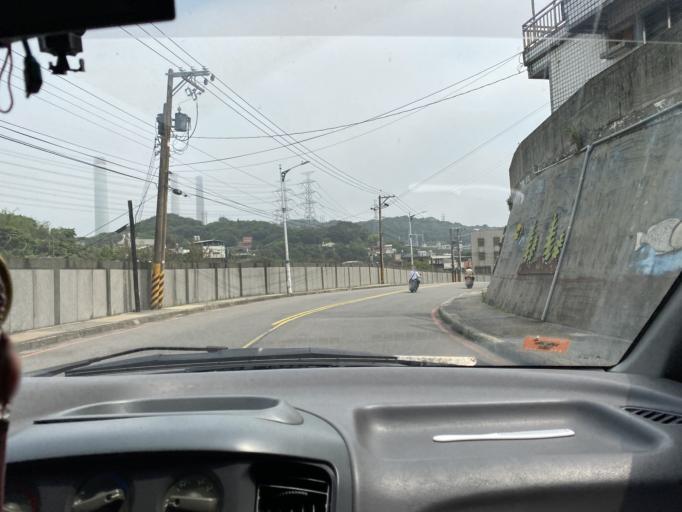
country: TW
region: Taiwan
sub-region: Keelung
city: Keelung
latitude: 25.1558
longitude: 121.7308
